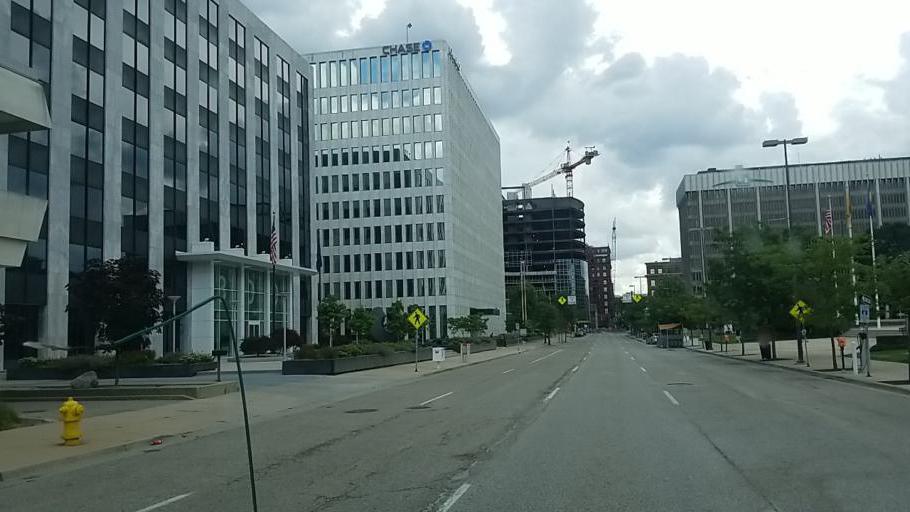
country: US
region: Michigan
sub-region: Kent County
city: Grand Rapids
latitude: 42.9696
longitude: -85.6701
